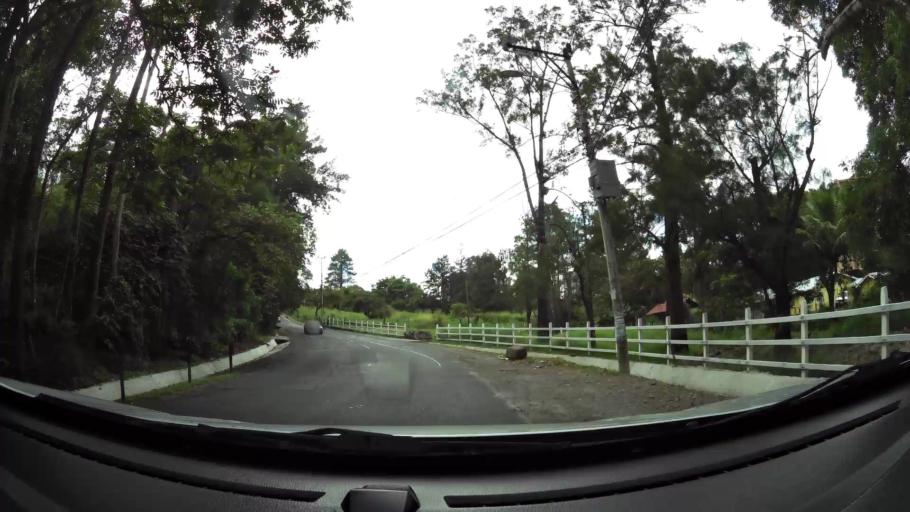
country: CR
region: San Jose
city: San Rafael
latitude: 9.9226
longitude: -84.1217
